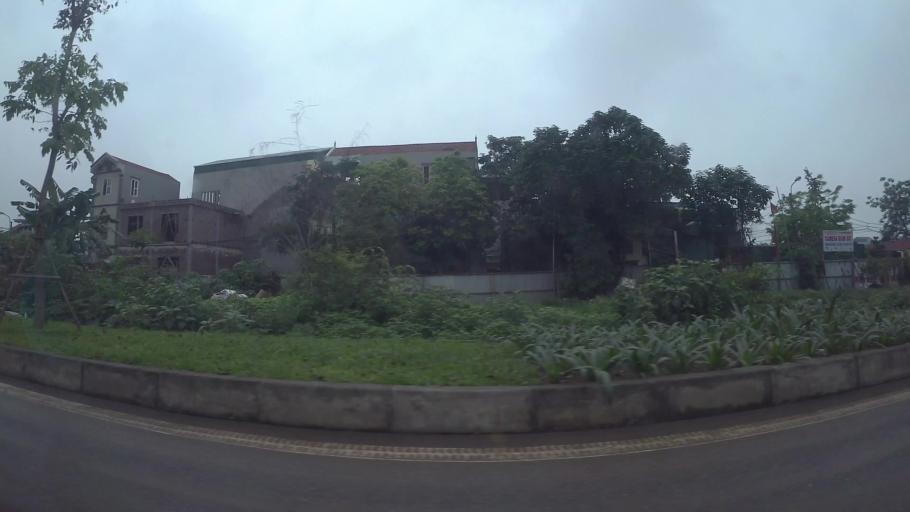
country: VN
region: Ha Noi
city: Van Dien
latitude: 20.9709
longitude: 105.8729
